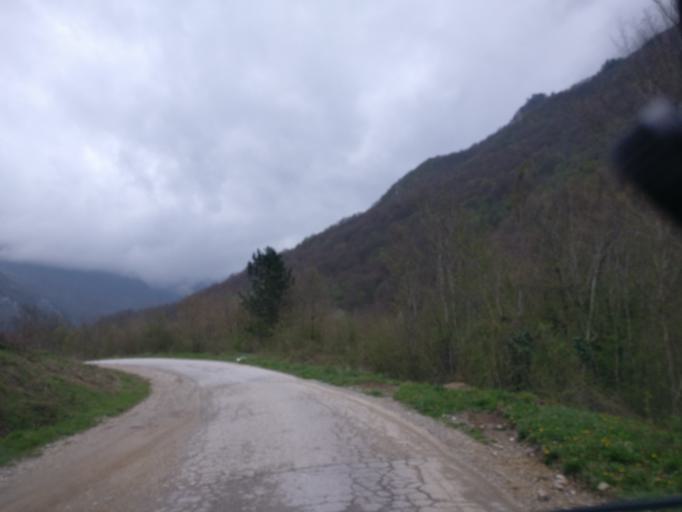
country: BA
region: Republika Srpska
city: Foca
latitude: 43.3522
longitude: 18.8270
